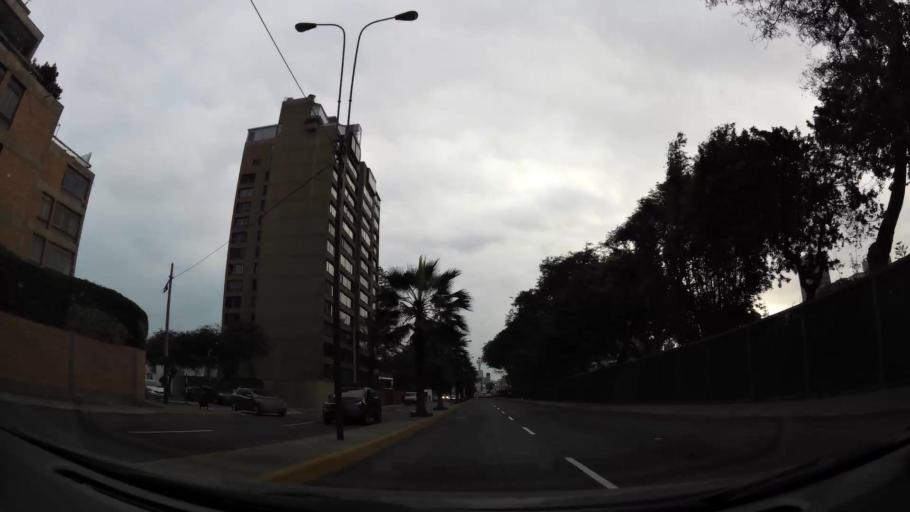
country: PE
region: Lima
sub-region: Lima
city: San Isidro
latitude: -12.1029
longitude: -77.0498
